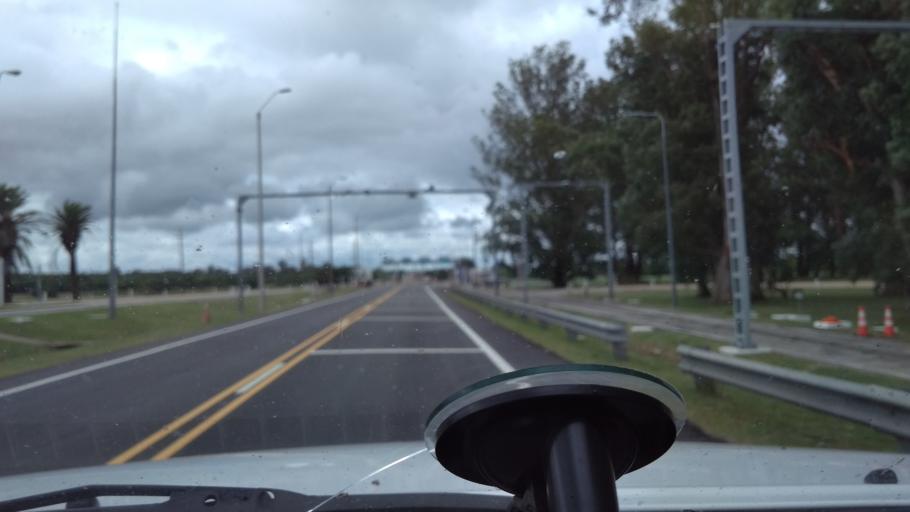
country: UY
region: Florida
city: Cardal
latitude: -34.3368
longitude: -56.2454
